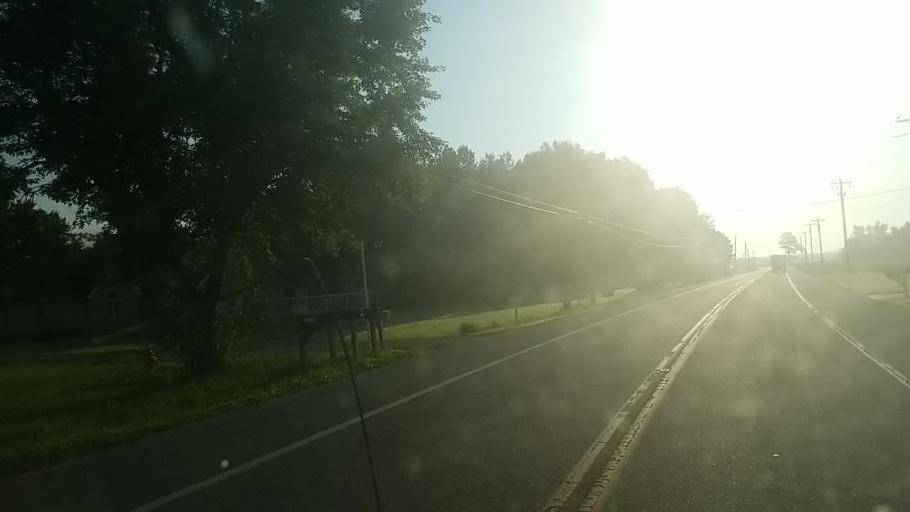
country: US
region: Delaware
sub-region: Sussex County
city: Selbyville
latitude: 38.4624
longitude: -75.1889
